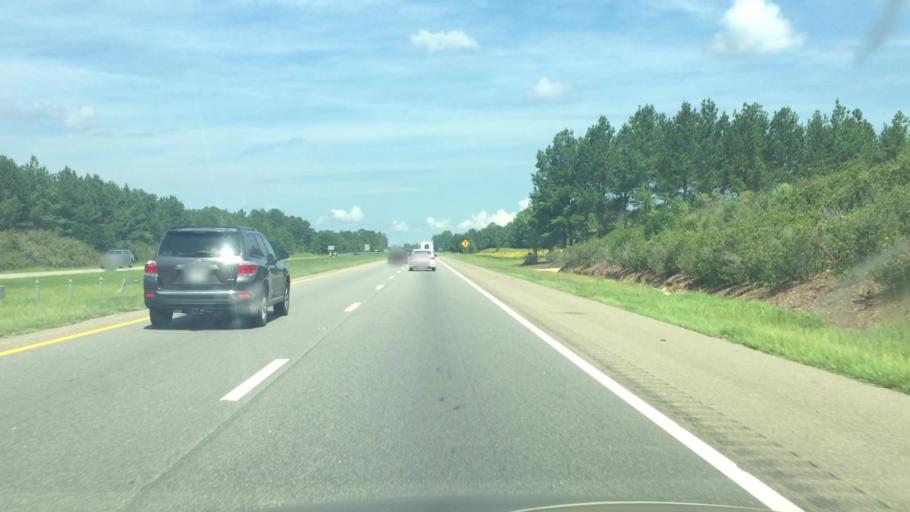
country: US
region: North Carolina
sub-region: Richmond County
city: Hamlet
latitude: 34.8587
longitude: -79.7431
